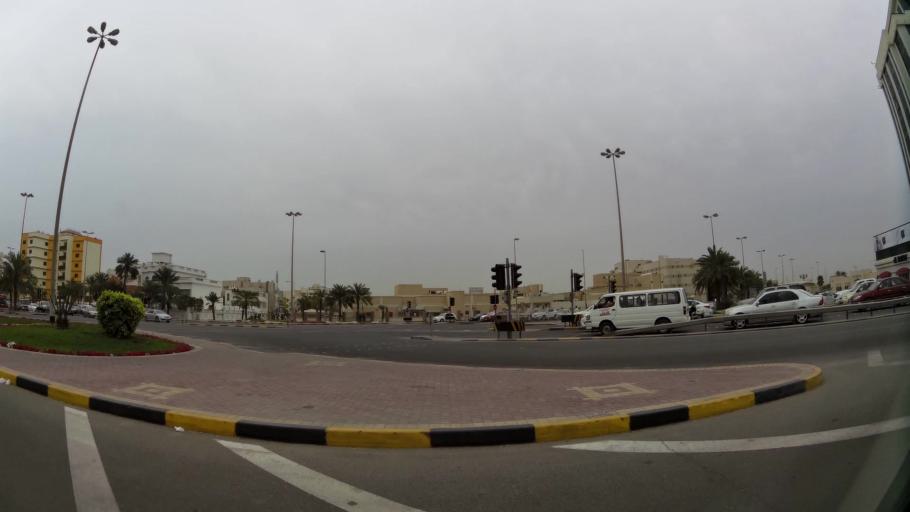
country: BH
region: Manama
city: Manama
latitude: 26.2188
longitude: 50.5663
